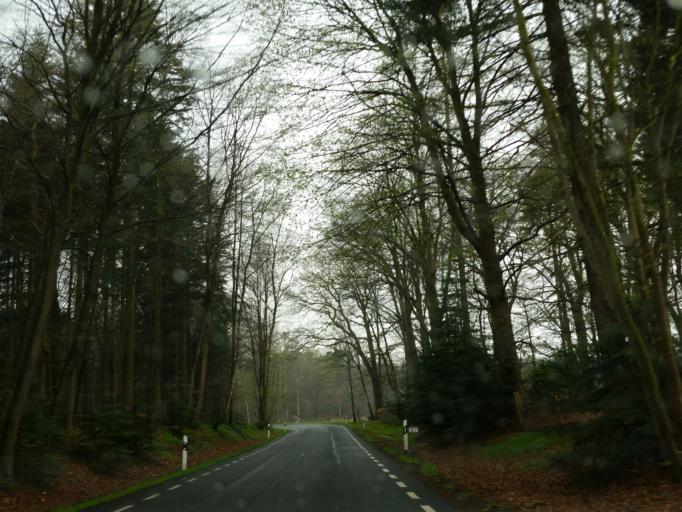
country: DE
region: Lower Saxony
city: Hipstedt
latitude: 53.5025
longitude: 8.9759
